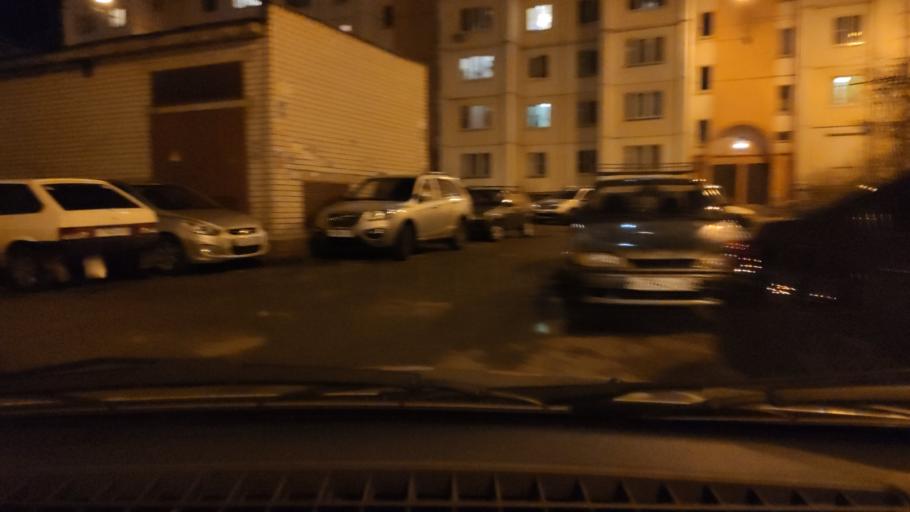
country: RU
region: Voronezj
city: Pridonskoy
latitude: 51.6260
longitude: 39.0769
